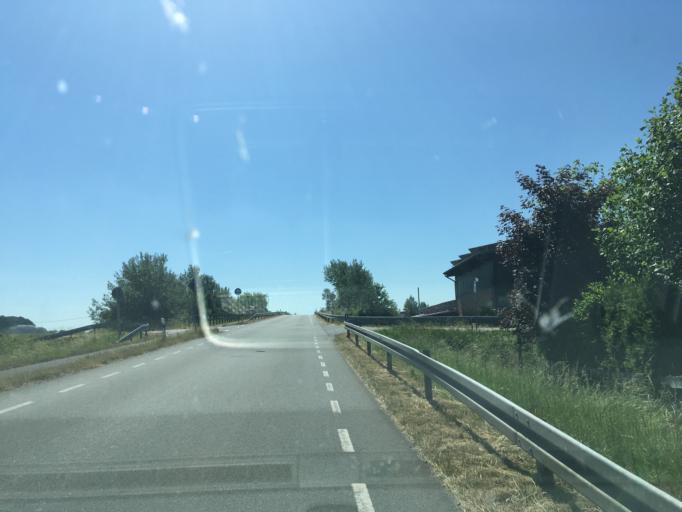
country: DE
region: North Rhine-Westphalia
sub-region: Regierungsbezirk Munster
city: Borken
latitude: 51.8275
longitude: 6.7977
